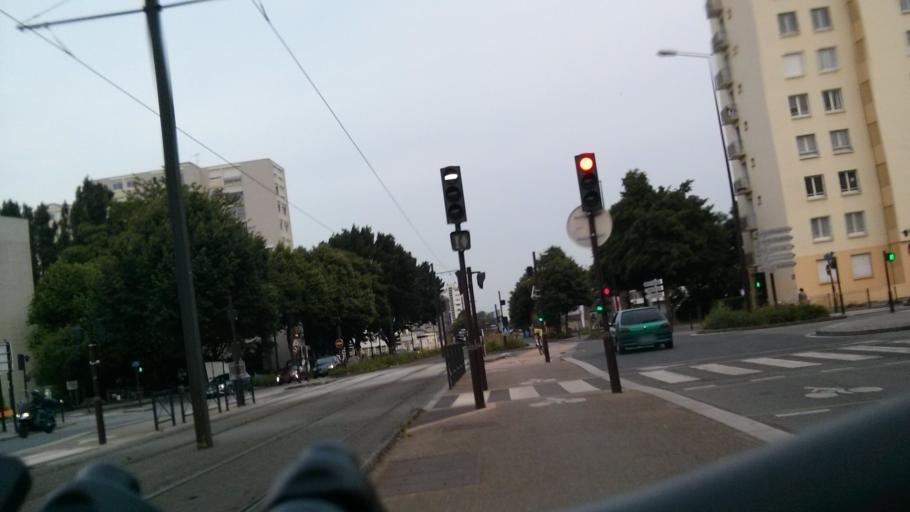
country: FR
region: Pays de la Loire
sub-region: Departement de la Loire-Atlantique
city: Nantes
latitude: 47.2057
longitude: -1.5477
